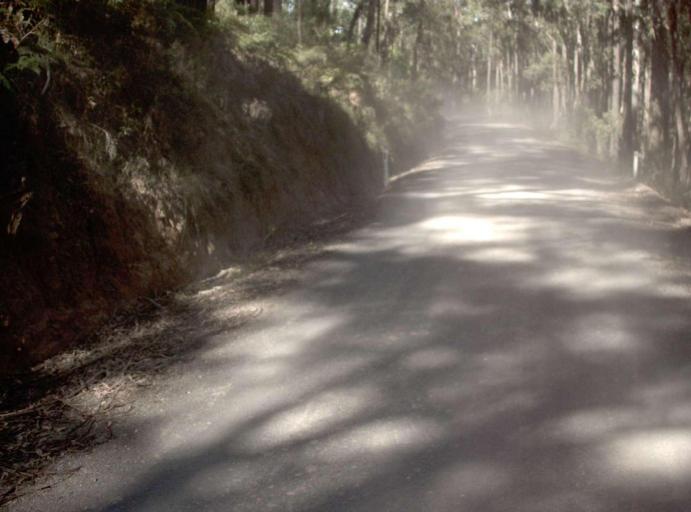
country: AU
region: New South Wales
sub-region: Bombala
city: Bombala
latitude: -37.2557
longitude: 148.7353
